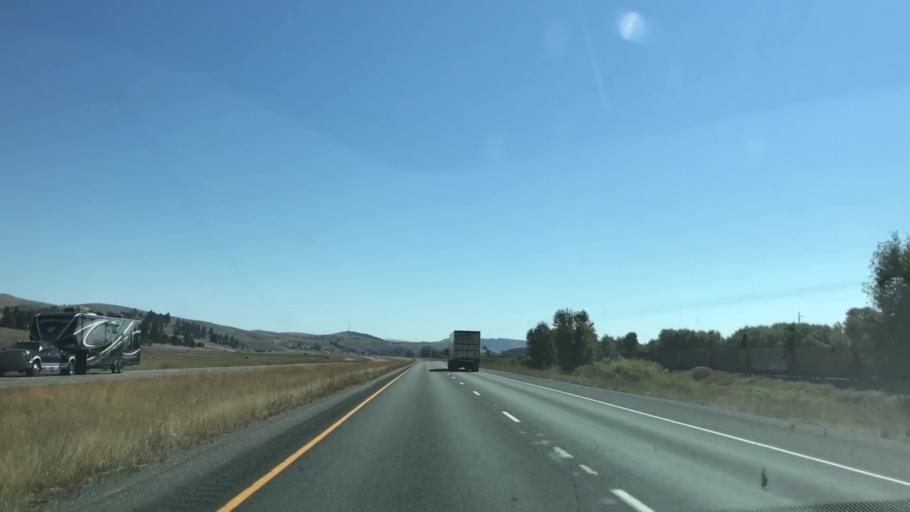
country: US
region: Montana
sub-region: Powell County
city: Deer Lodge
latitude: 46.6030
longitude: -112.9657
